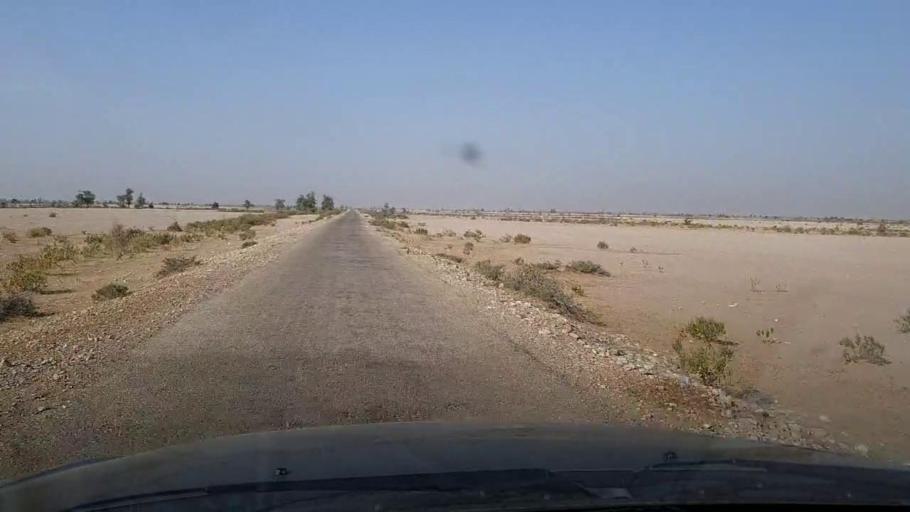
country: PK
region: Sindh
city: Sann
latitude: 25.9910
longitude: 68.0698
